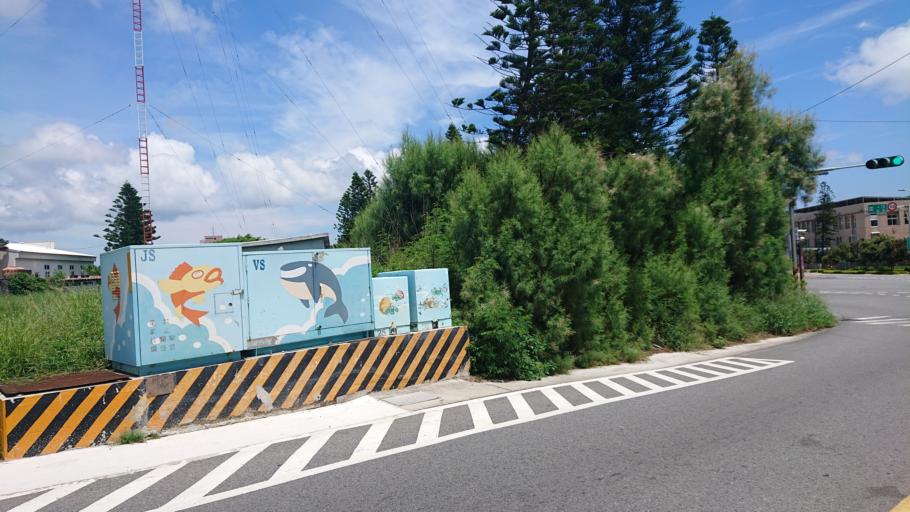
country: TW
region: Taiwan
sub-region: Penghu
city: Ma-kung
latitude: 23.5703
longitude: 119.5818
